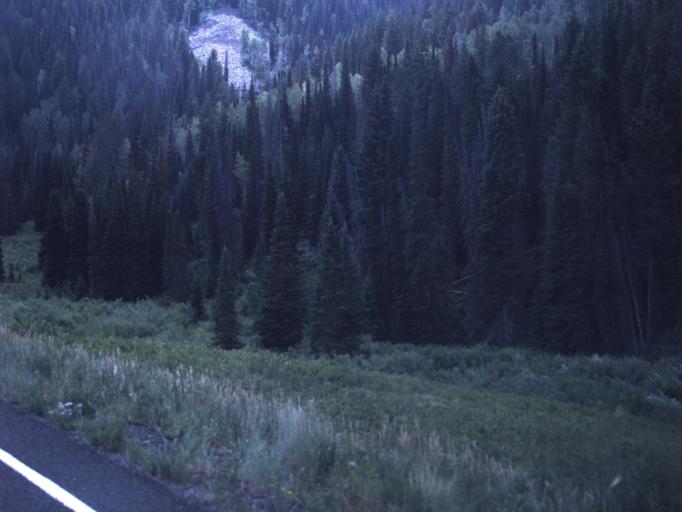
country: US
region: Utah
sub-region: Summit County
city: Francis
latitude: 40.5236
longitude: -111.0914
